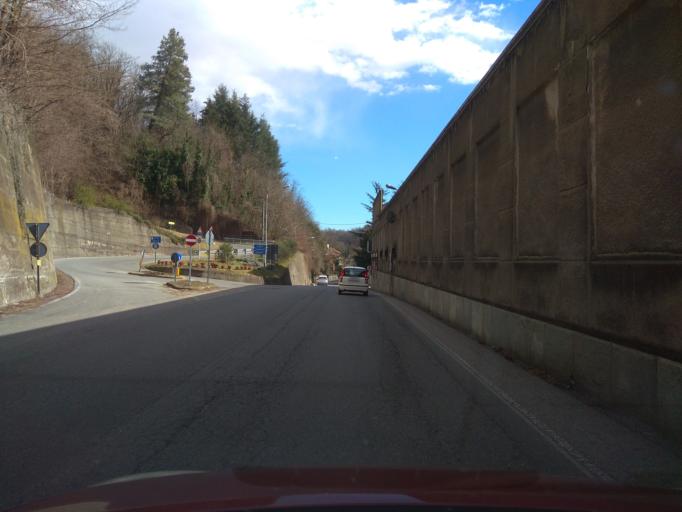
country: IT
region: Piedmont
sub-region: Provincia di Biella
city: Fontanella-Ozino
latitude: 45.6144
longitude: 8.1645
